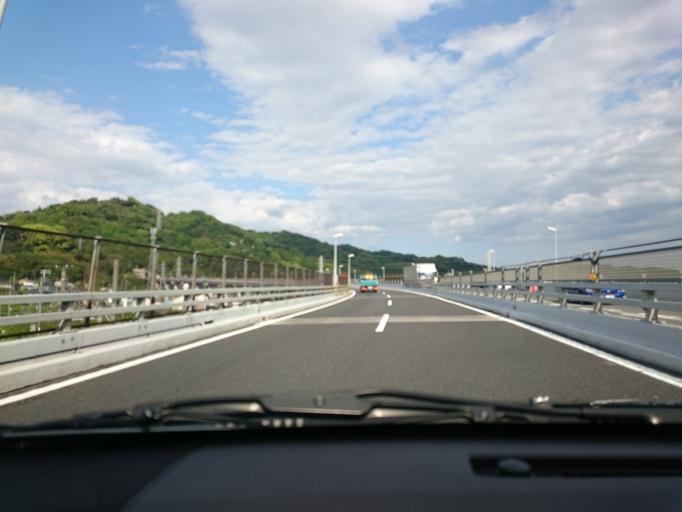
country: JP
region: Kanagawa
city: Odawara
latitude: 35.2899
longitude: 139.1972
